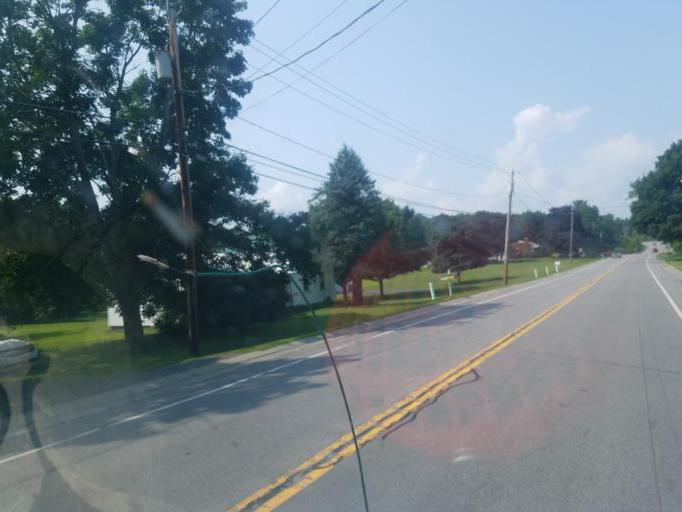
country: US
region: New York
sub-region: Montgomery County
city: Fonda
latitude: 42.9660
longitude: -74.3878
